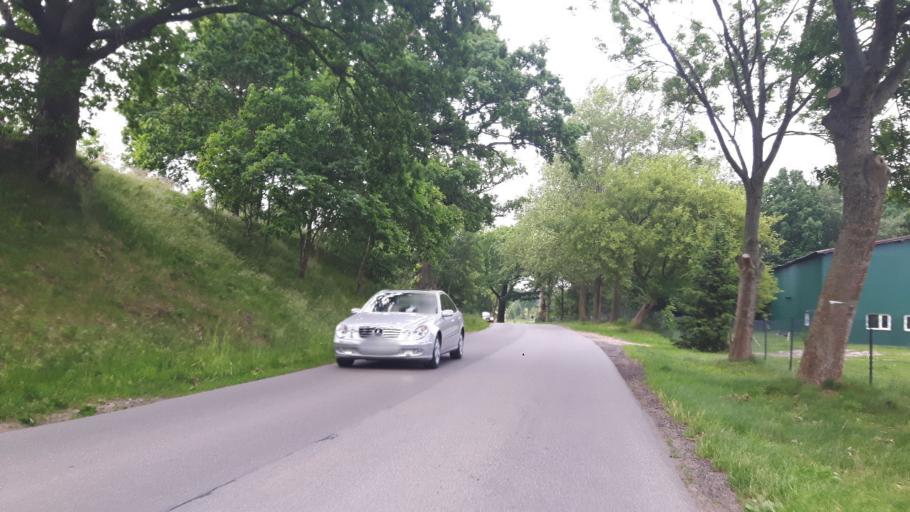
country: PL
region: Pomeranian Voivodeship
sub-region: Slupsk
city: Slupsk
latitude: 54.6255
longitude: 17.0251
